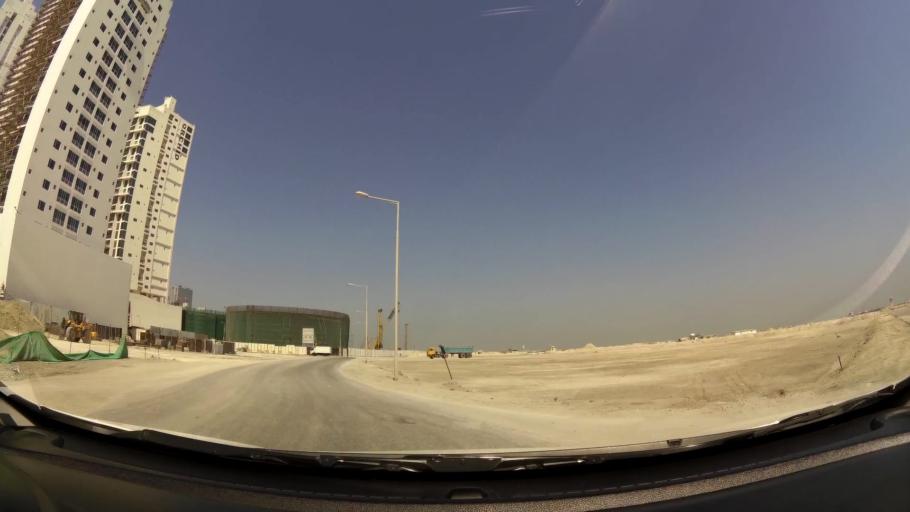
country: BH
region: Manama
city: Manama
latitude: 26.2145
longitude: 50.6202
